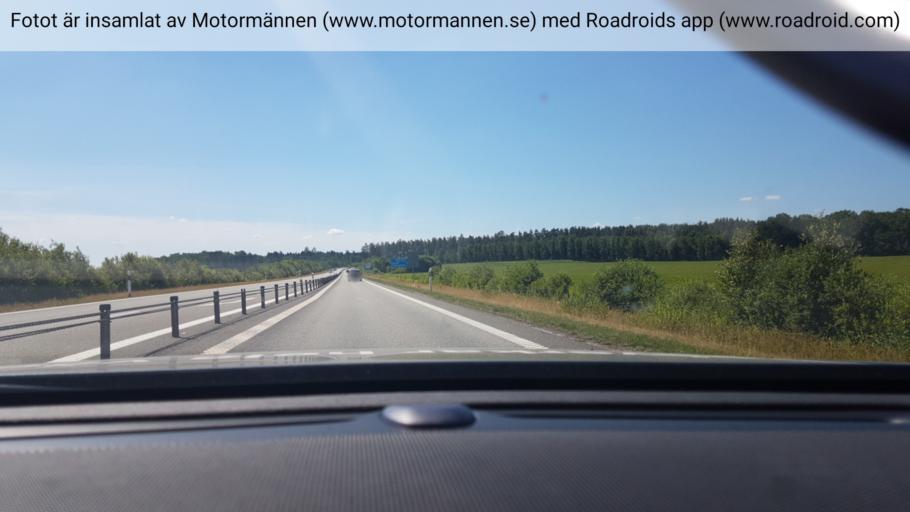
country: SE
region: Skane
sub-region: Hassleholms Kommun
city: Hassleholm
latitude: 56.1818
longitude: 13.8442
